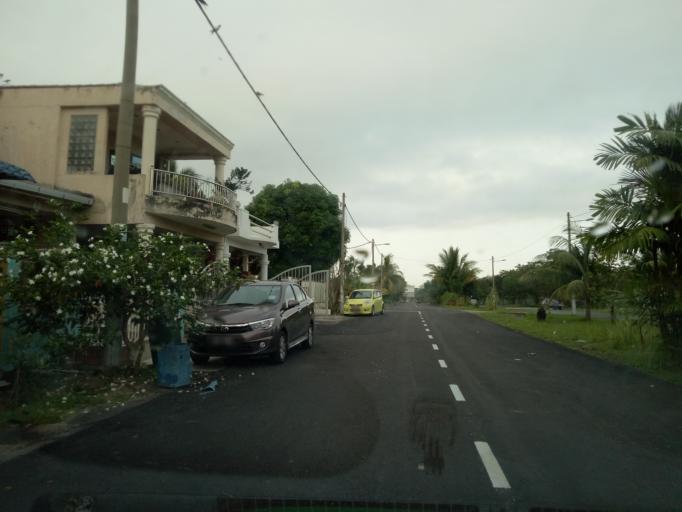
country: MY
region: Selangor
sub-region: Hulu Langat
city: Semenyih
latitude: 2.9311
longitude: 101.8612
